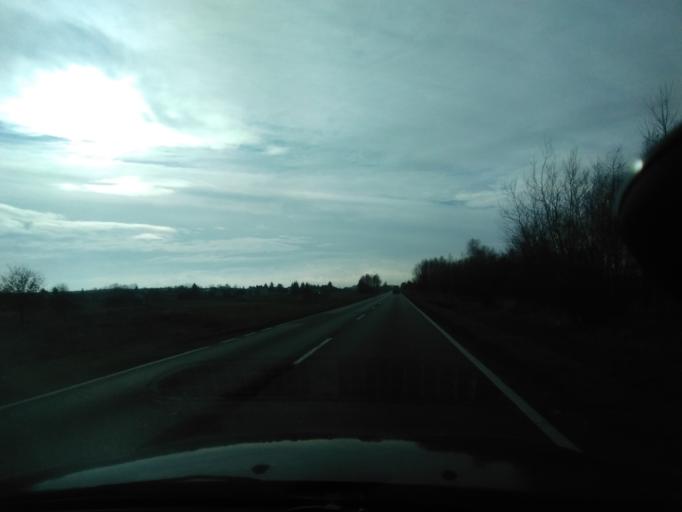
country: PL
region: Subcarpathian Voivodeship
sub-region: Powiat krosnienski
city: Kroscienko Wyzne
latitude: 49.6649
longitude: 21.8430
